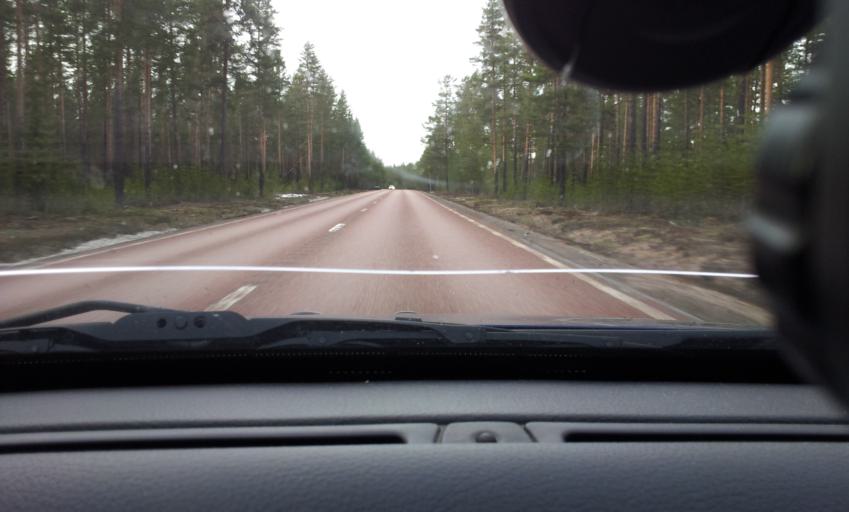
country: SE
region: Gaevleborg
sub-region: Ljusdals Kommun
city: Farila
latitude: 61.9087
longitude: 15.6297
